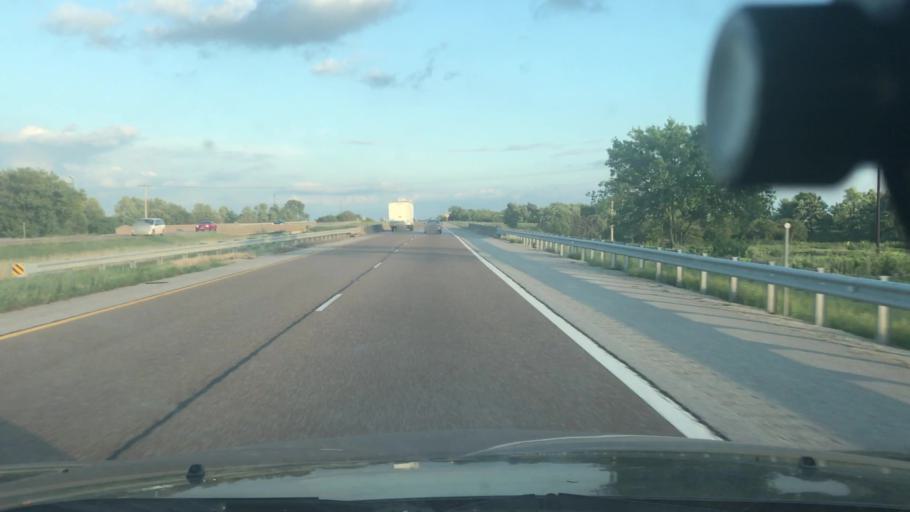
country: US
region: Illinois
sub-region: Clinton County
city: New Baden
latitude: 38.5360
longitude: -89.7294
